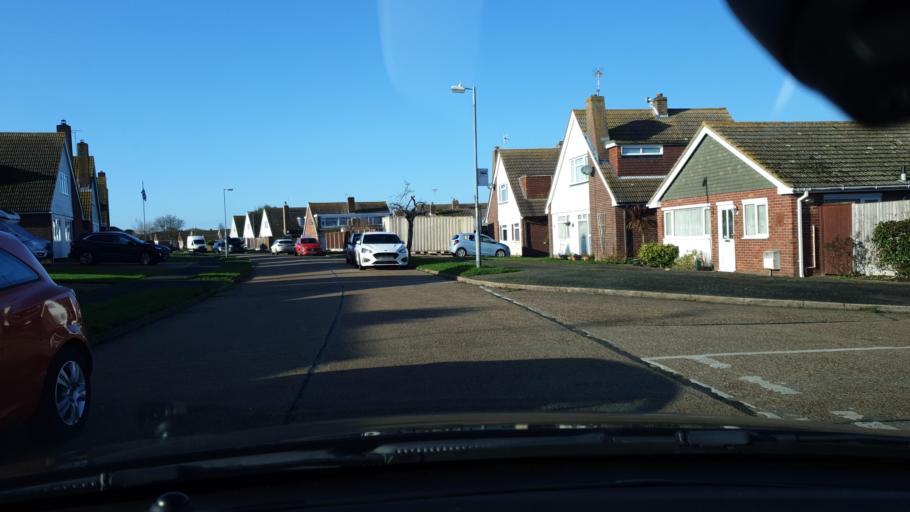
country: GB
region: England
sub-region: Essex
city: Clacton-on-Sea
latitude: 51.8098
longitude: 1.1948
